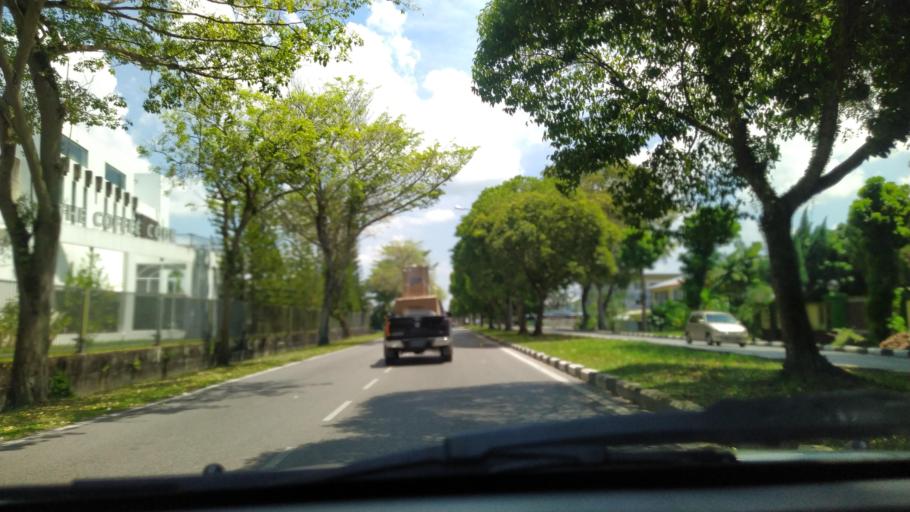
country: MY
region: Sarawak
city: Sibu
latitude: 2.3044
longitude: 111.8315
